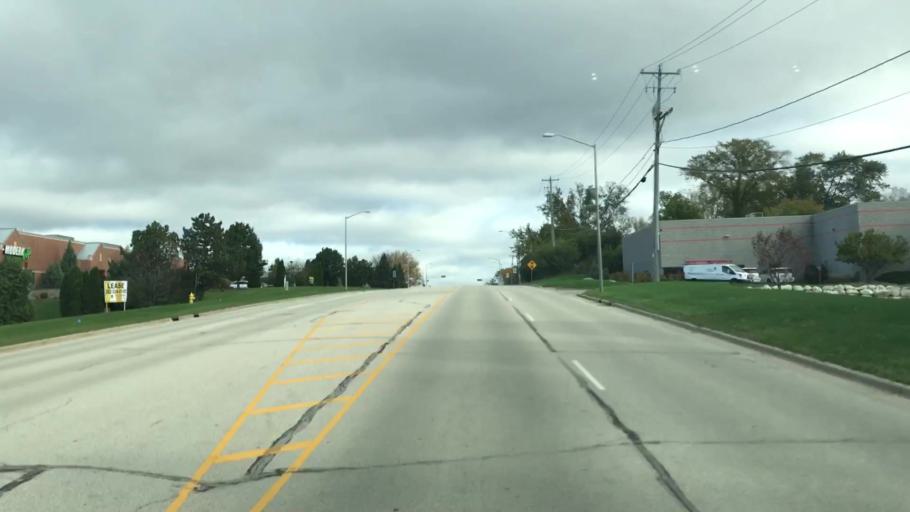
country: US
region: Wisconsin
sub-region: Waukesha County
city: Waukesha
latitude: 43.0295
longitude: -88.2259
